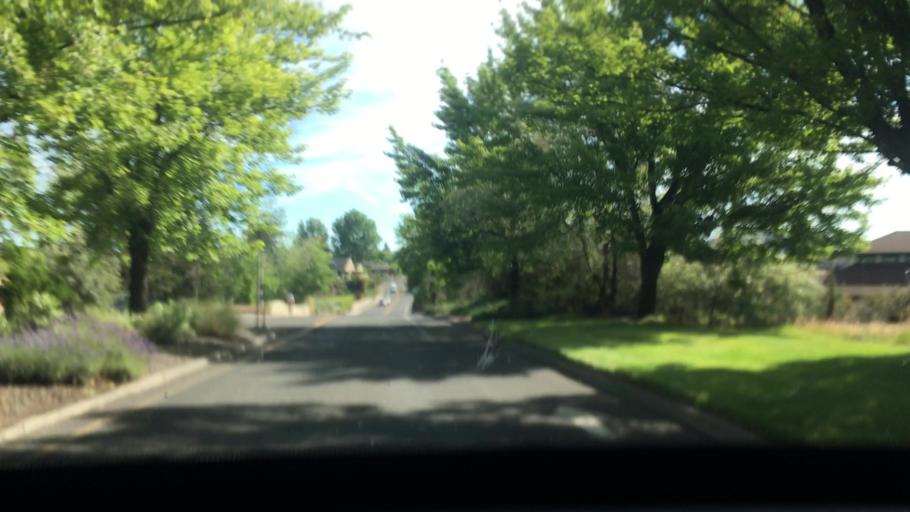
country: US
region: Oregon
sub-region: Deschutes County
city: Bend
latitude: 44.0485
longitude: -121.3224
